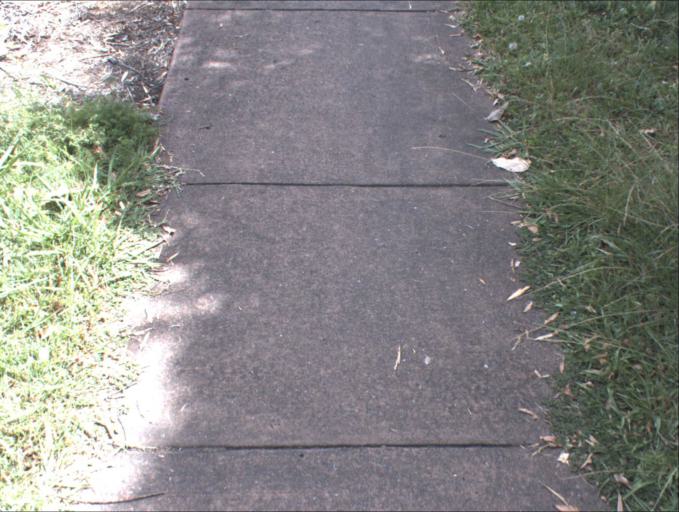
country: AU
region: Queensland
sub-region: Logan
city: Slacks Creek
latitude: -27.6636
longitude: 153.1431
